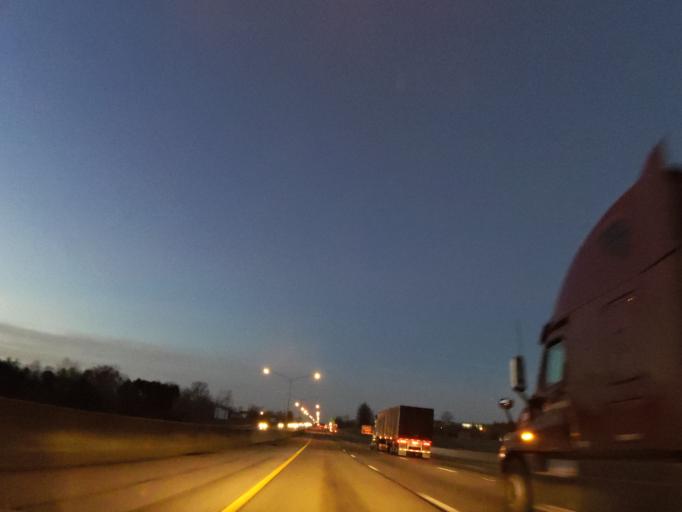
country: US
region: Kentucky
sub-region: Laurel County
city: London
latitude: 37.1232
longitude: -84.1065
